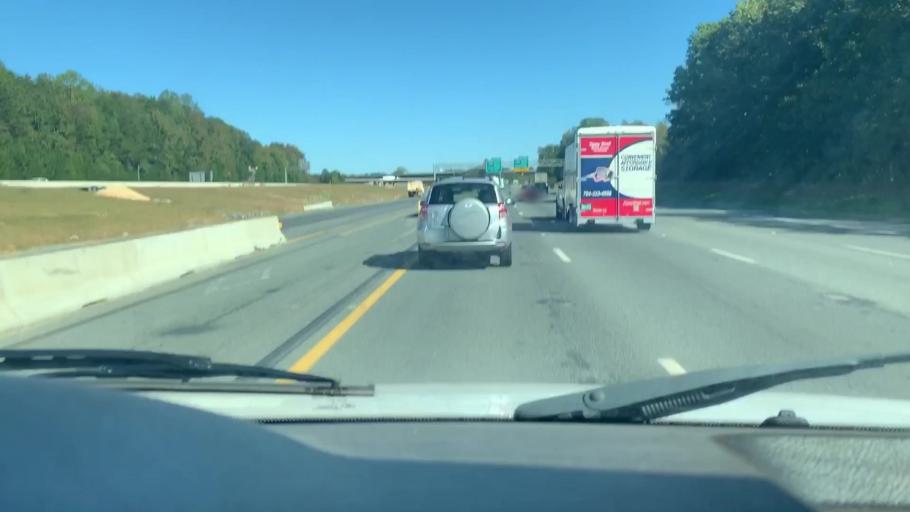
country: US
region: North Carolina
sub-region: Mecklenburg County
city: Huntersville
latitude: 35.3559
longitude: -80.8442
